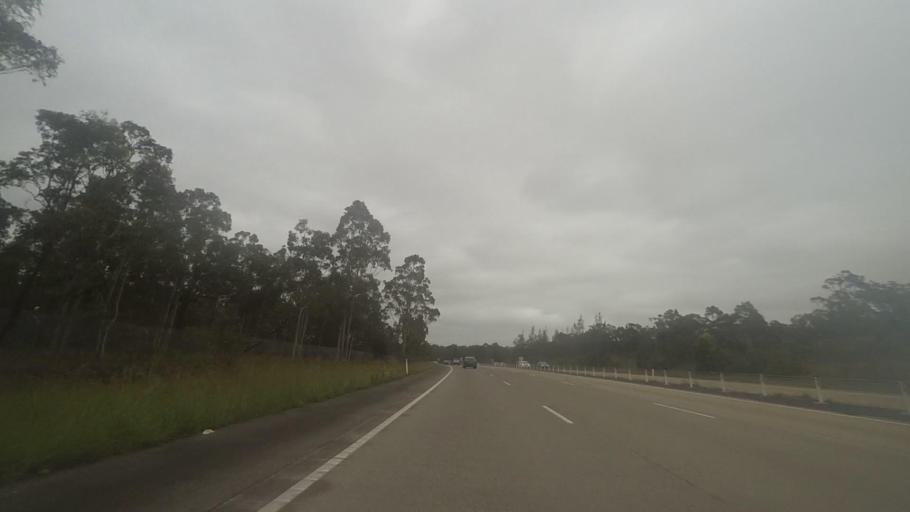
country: AU
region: New South Wales
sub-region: Port Stephens Shire
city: Medowie
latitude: -32.6841
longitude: 151.8122
